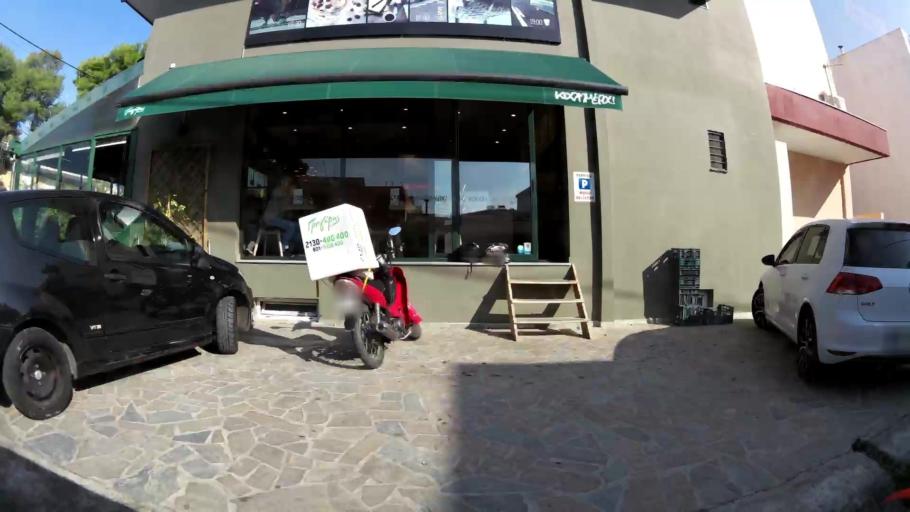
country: GR
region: Attica
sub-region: Nomarchia Athinas
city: Nea Filadelfeia
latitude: 38.0567
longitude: 23.7378
